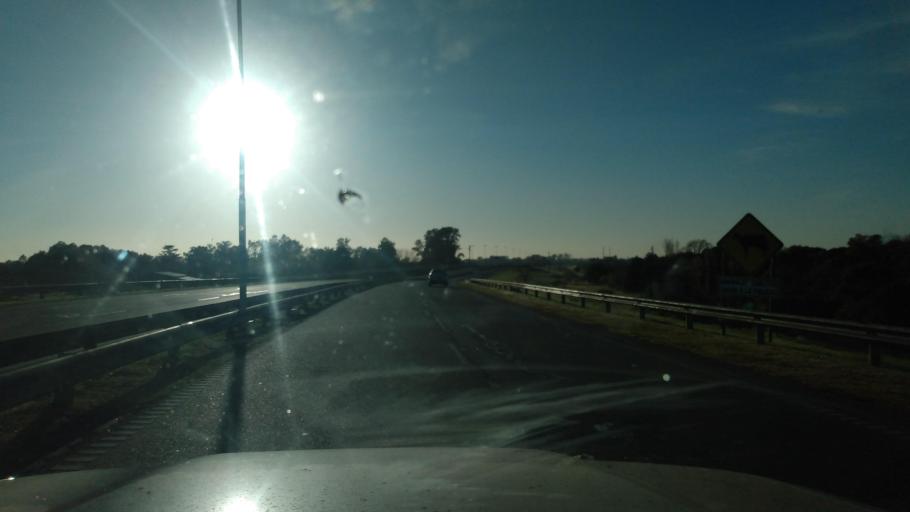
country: AR
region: Buenos Aires
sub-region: Partido de Lujan
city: Lujan
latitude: -34.5454
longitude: -59.1616
